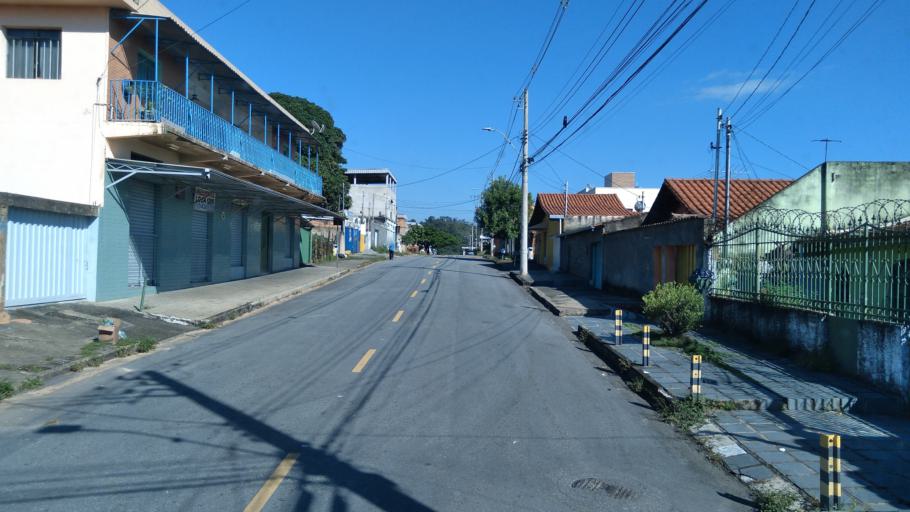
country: BR
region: Minas Gerais
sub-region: Santa Luzia
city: Santa Luzia
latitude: -19.8283
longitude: -43.8999
